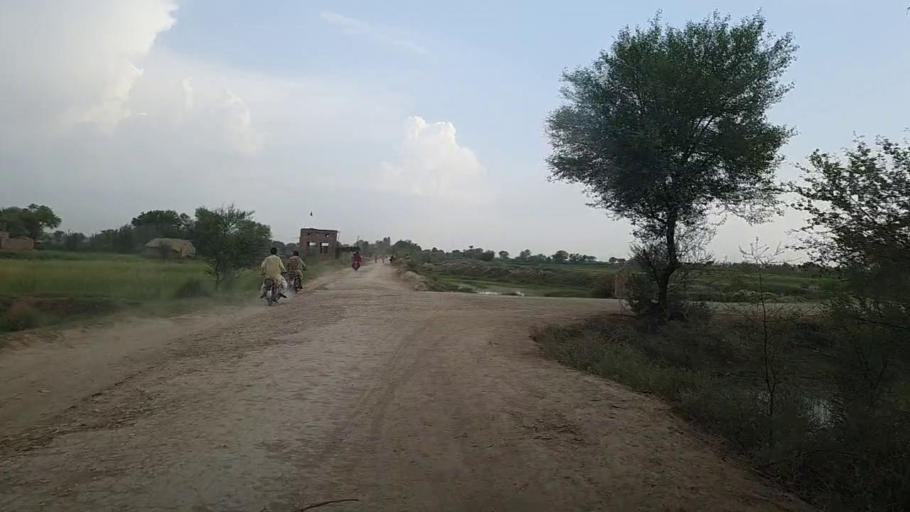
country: PK
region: Sindh
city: Khanpur
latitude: 27.8569
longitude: 69.4866
